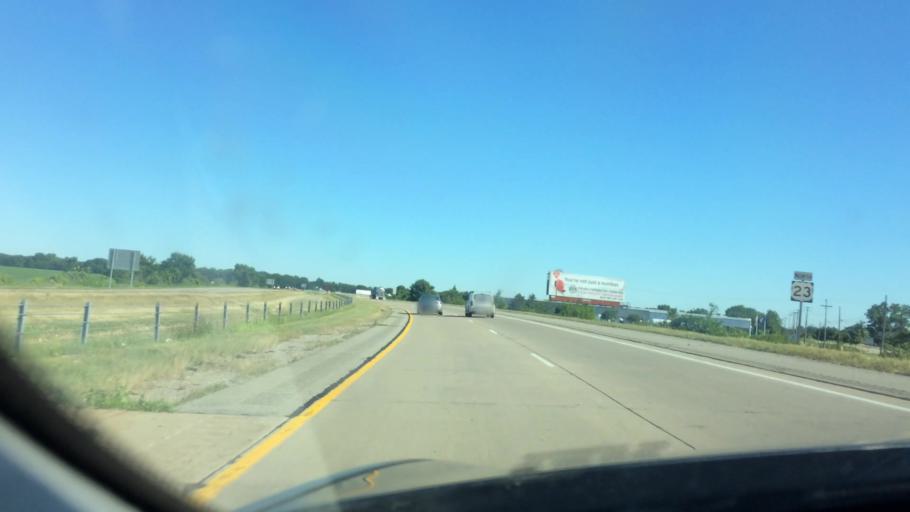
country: US
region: Michigan
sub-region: Monroe County
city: Dundee
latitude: 41.9661
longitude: -83.6729
